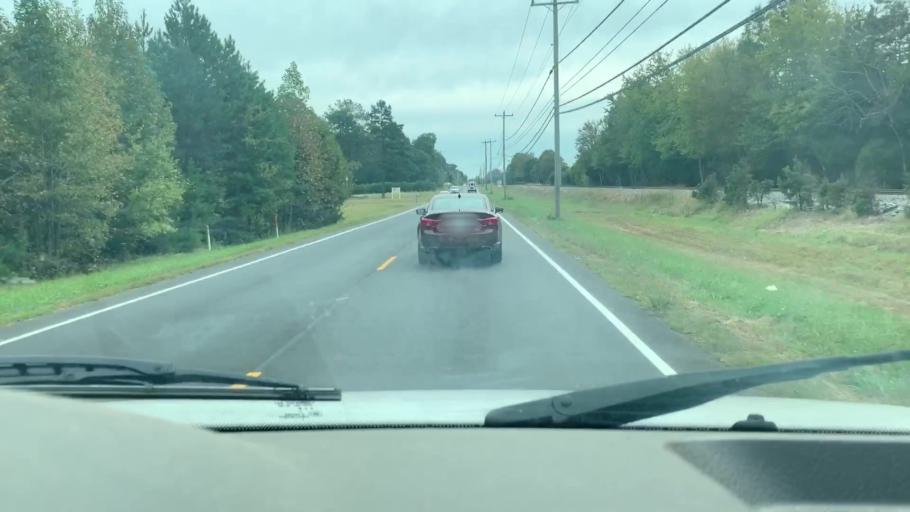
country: US
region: North Carolina
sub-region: Gaston County
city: Davidson
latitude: 35.5267
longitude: -80.8437
